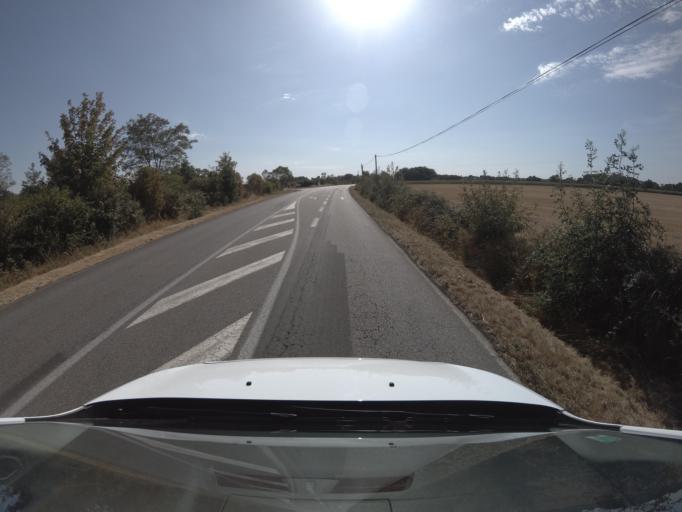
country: FR
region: Poitou-Charentes
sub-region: Departement des Deux-Sevres
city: Mauze-Thouarsais
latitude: 47.0044
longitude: -0.3529
